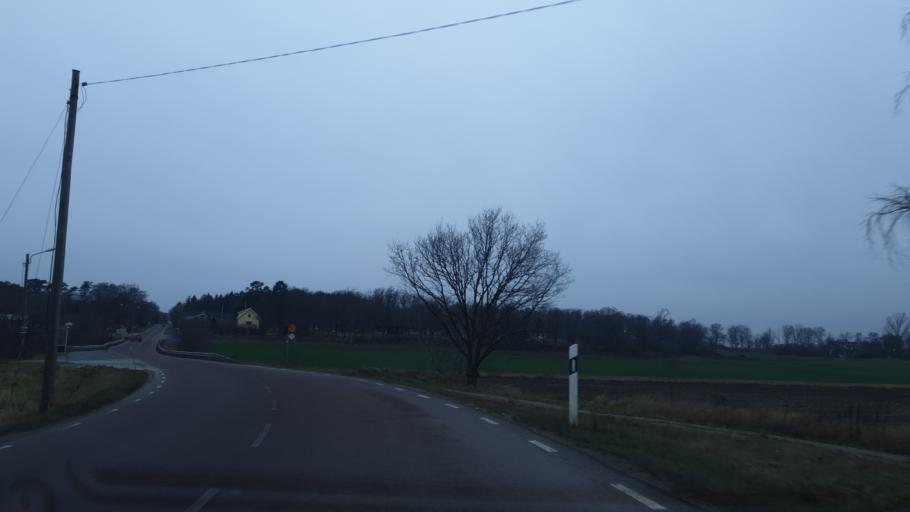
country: SE
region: Blekinge
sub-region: Karlskrona Kommun
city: Jaemjoe
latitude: 56.1668
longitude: 15.7590
